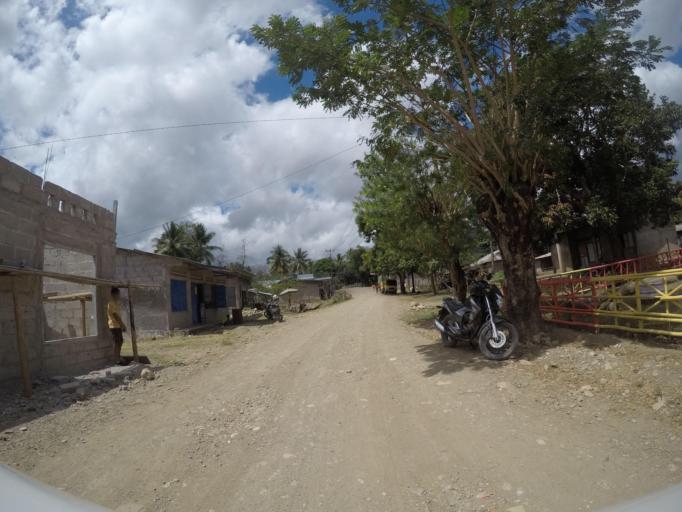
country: TL
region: Lautem
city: Lospalos
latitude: -8.5105
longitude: 126.8325
